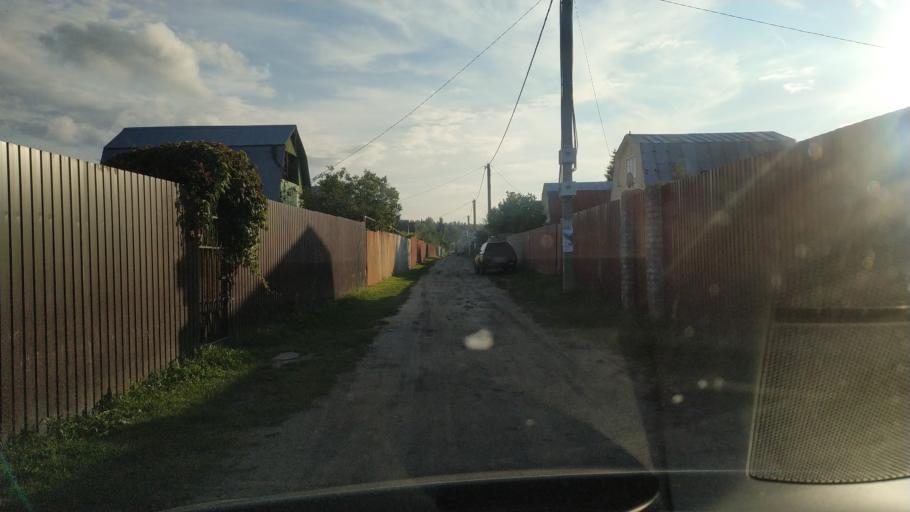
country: RU
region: Moskovskaya
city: Roshal'
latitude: 55.6442
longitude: 39.7936
